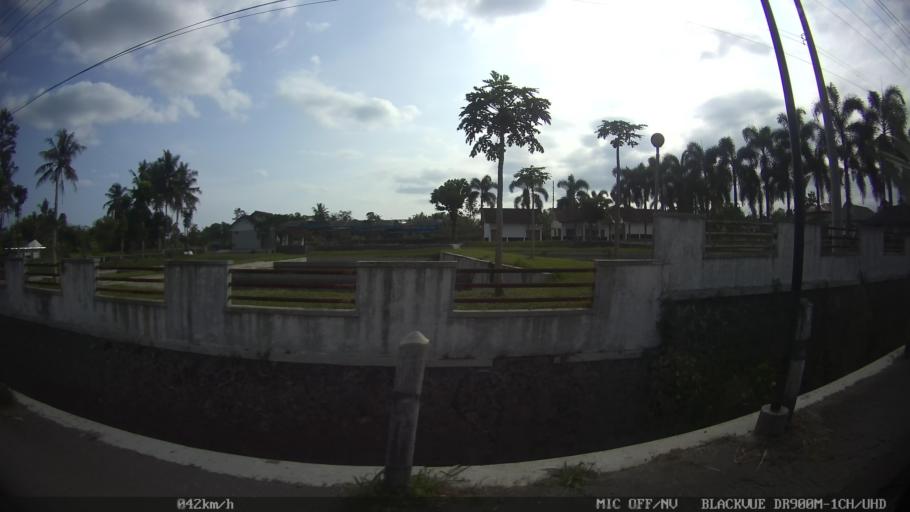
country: ID
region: Central Java
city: Candi Prambanan
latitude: -7.6920
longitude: 110.4628
